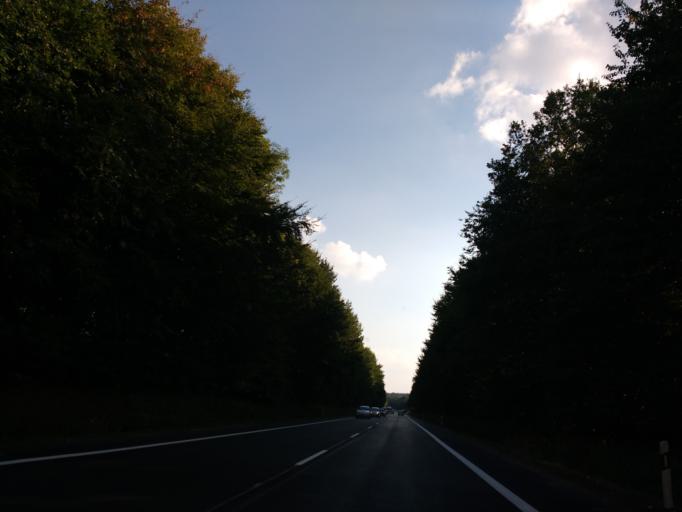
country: DE
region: North Rhine-Westphalia
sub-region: Regierungsbezirk Detmold
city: Blomberg
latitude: 51.9229
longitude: 9.0855
